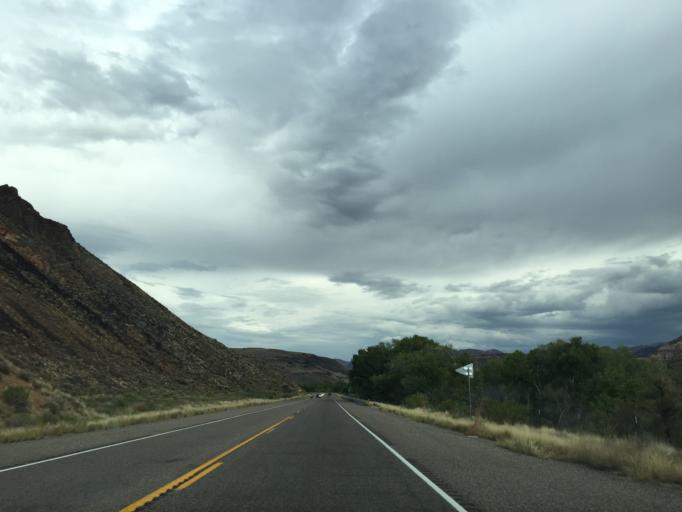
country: US
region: Utah
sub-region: Washington County
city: LaVerkin
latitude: 37.1824
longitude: -113.1325
